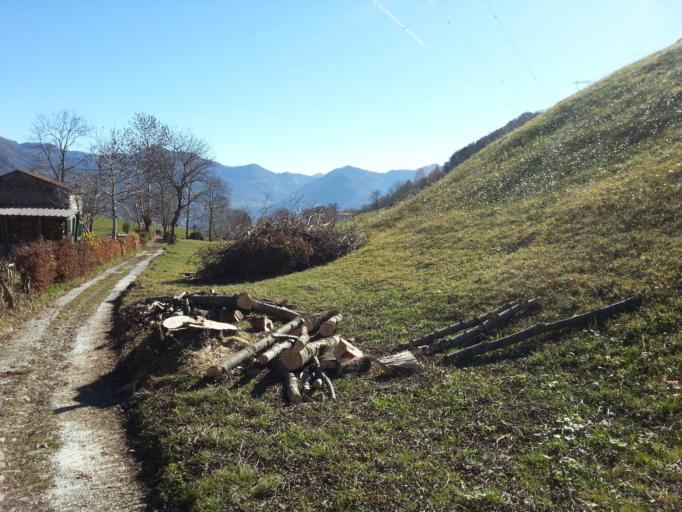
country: IT
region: Lombardy
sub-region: Provincia di Lecco
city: Primaluna
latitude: 45.9672
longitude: 9.4286
